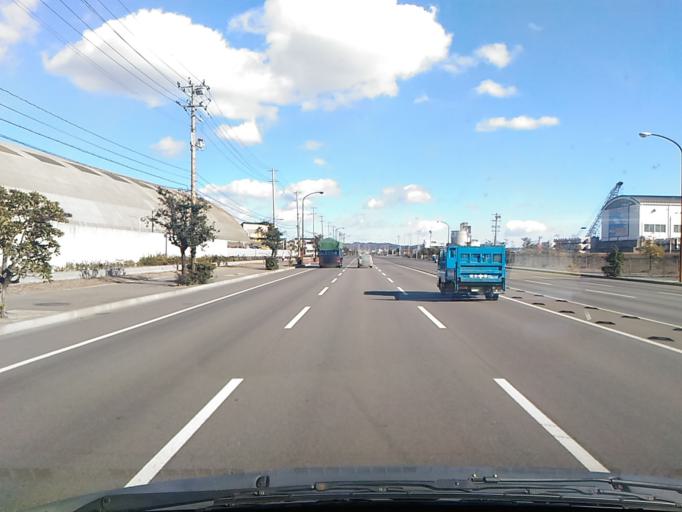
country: JP
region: Fukushima
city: Iwaki
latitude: 36.9387
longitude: 140.8834
